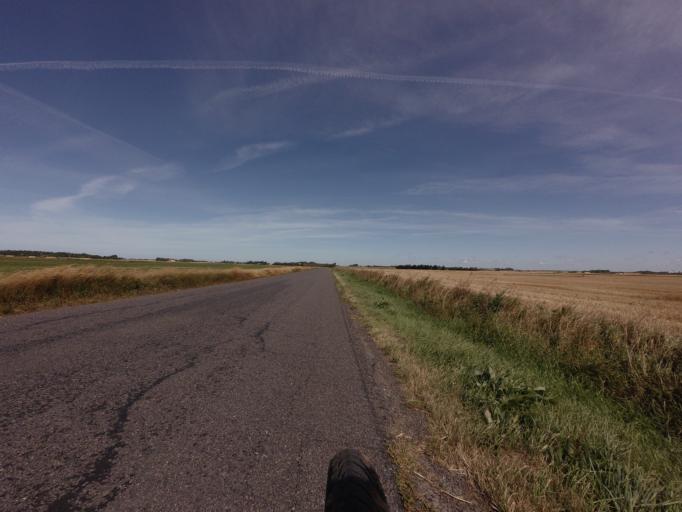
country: DK
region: North Denmark
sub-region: Bronderslev Kommune
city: Bronderslev
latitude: 57.3121
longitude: 9.8115
